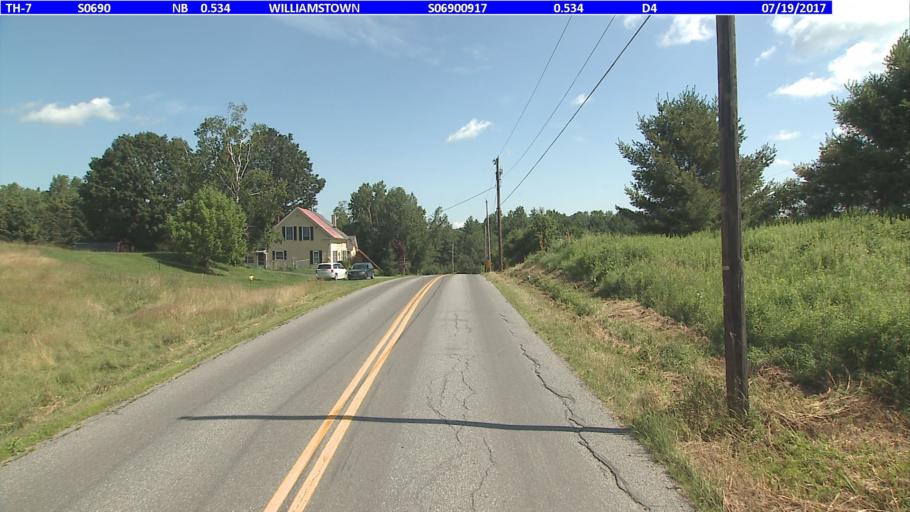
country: US
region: Vermont
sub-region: Washington County
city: South Barre
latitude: 44.1396
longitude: -72.4918
